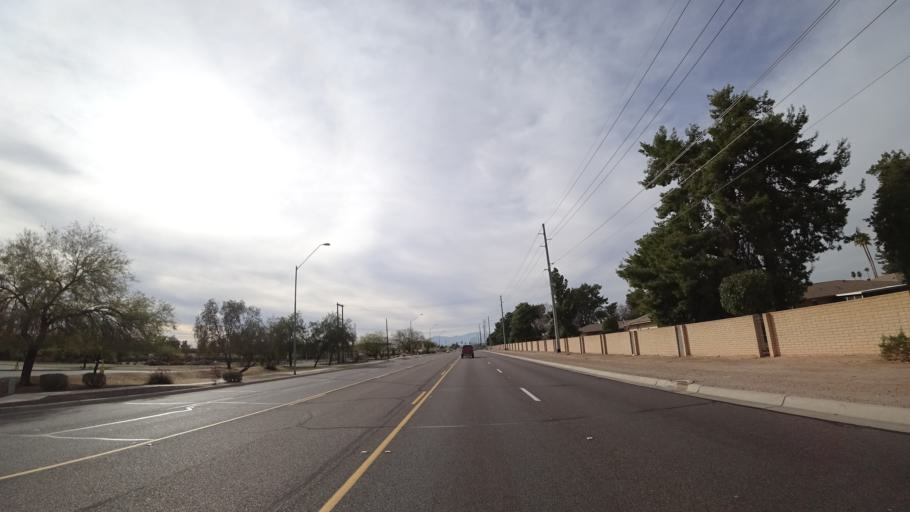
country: US
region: Arizona
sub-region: Maricopa County
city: Youngtown
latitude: 33.5657
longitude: -112.2952
